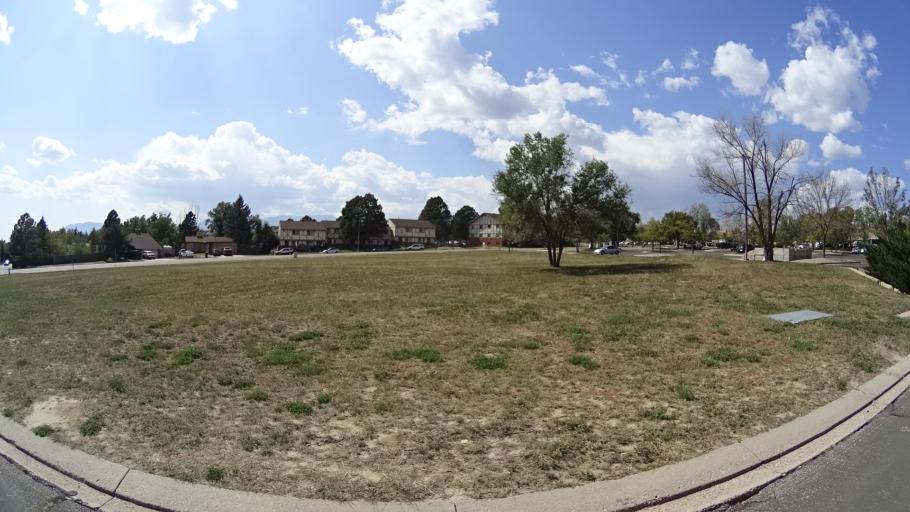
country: US
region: Colorado
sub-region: El Paso County
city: Cimarron Hills
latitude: 38.8768
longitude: -104.7530
